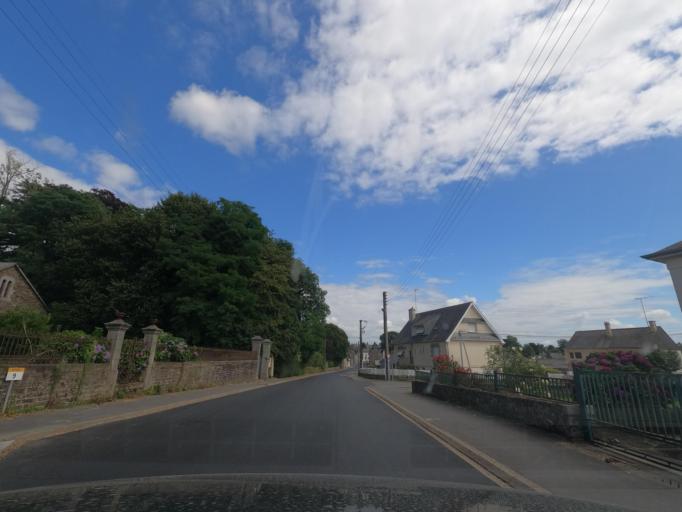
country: FR
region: Pays de la Loire
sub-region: Departement de la Mayenne
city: Fougerolles-du-Plessis
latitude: 48.4752
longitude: -0.9780
